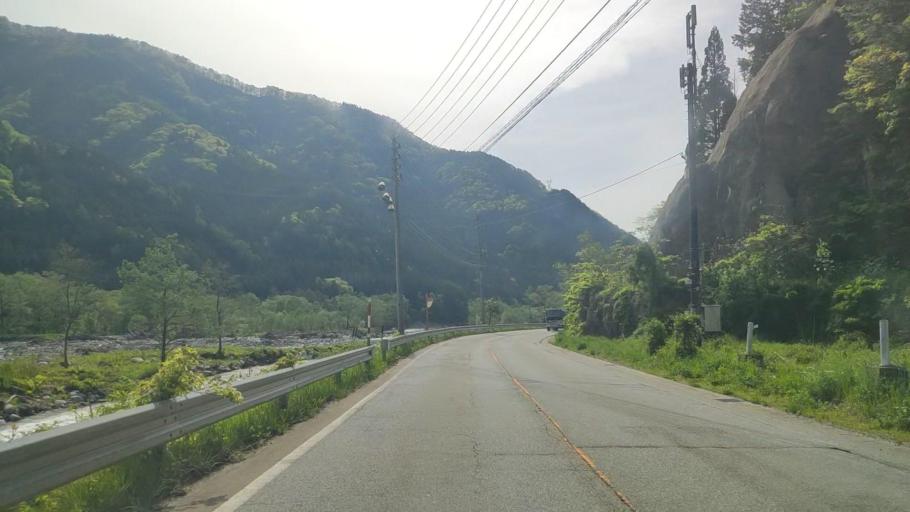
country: JP
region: Gifu
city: Takayama
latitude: 36.2492
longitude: 137.4876
